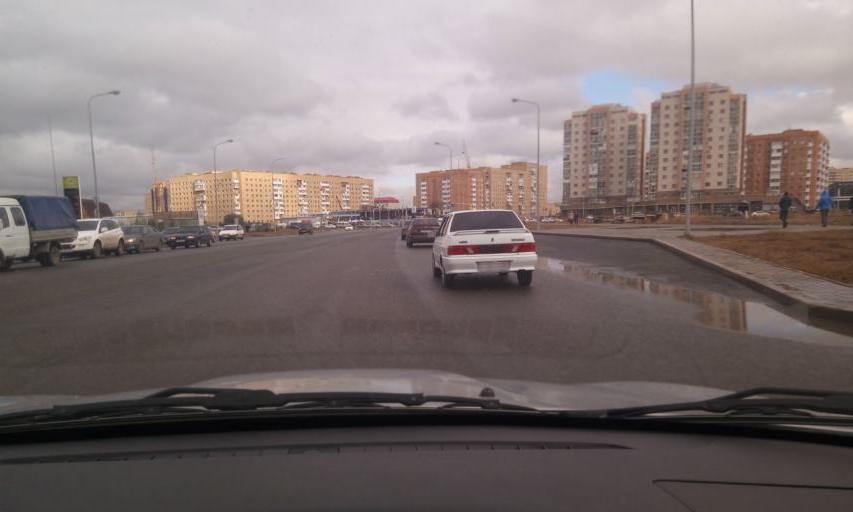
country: KZ
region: Astana Qalasy
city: Astana
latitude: 51.1717
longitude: 71.3739
